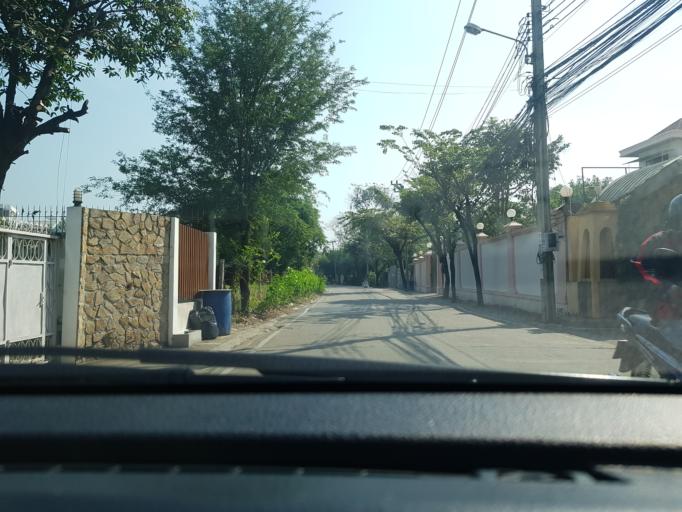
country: TH
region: Bangkok
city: Bangkok Yai
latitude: 13.7303
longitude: 100.4567
